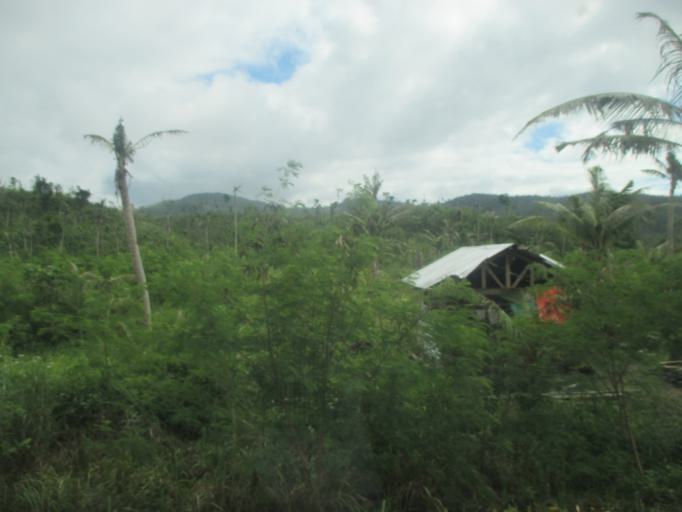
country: PH
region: Eastern Visayas
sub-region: Province of Eastern Samar
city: Lawa-an
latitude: 11.1010
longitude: 125.2095
